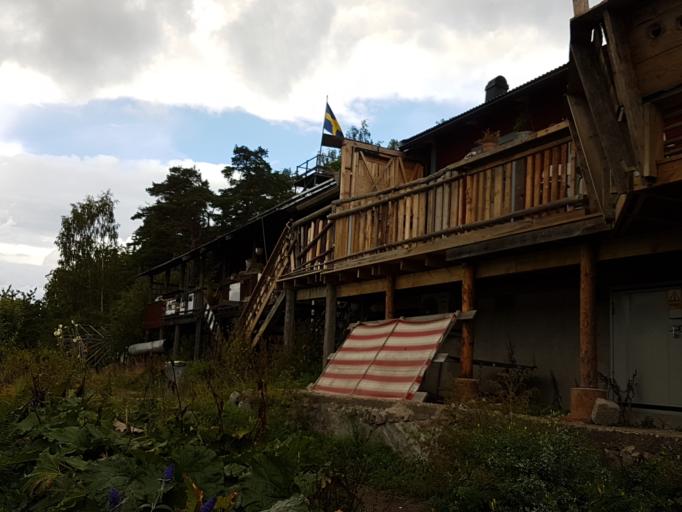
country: SE
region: Stockholm
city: Stenhamra
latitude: 59.2947
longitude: 17.7167
